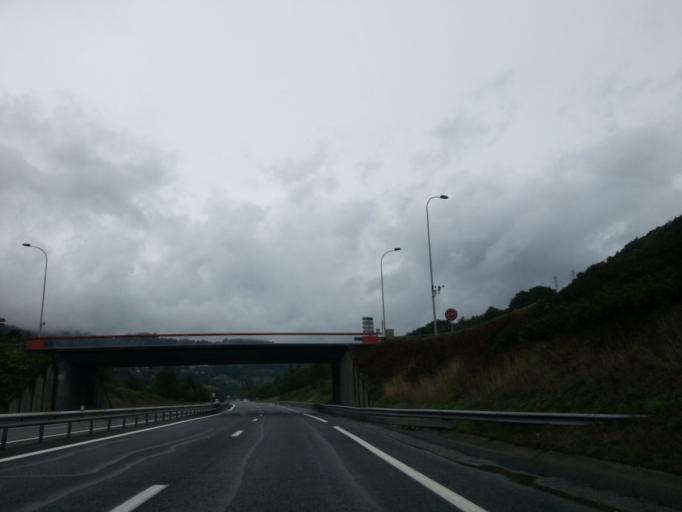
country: FR
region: Rhone-Alpes
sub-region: Departement de la Savoie
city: Marthod
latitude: 45.7032
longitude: 6.4062
